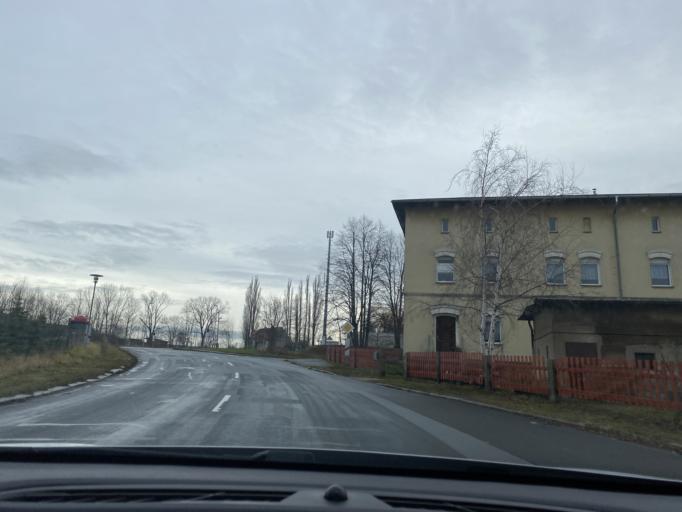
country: DE
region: Saxony
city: Reichenbach
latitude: 51.1364
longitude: 14.7977
